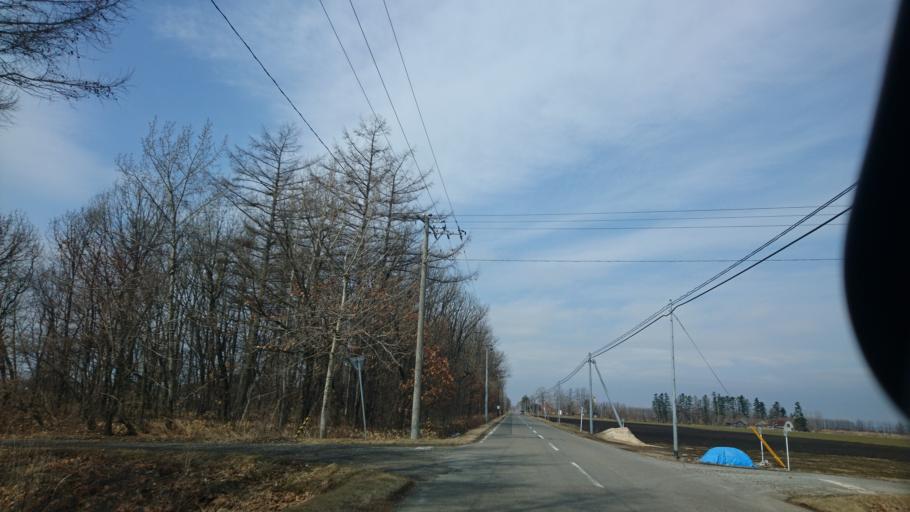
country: JP
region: Hokkaido
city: Otofuke
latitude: 43.0799
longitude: 143.2331
